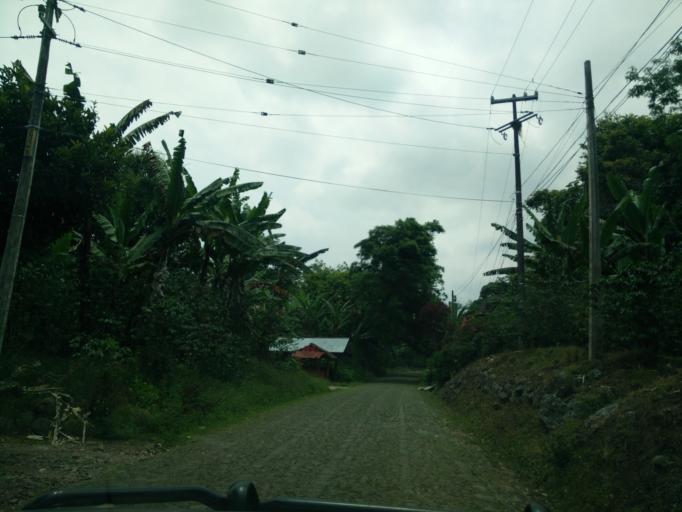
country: MX
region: Veracruz
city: Xico
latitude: 19.4112
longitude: -96.9924
